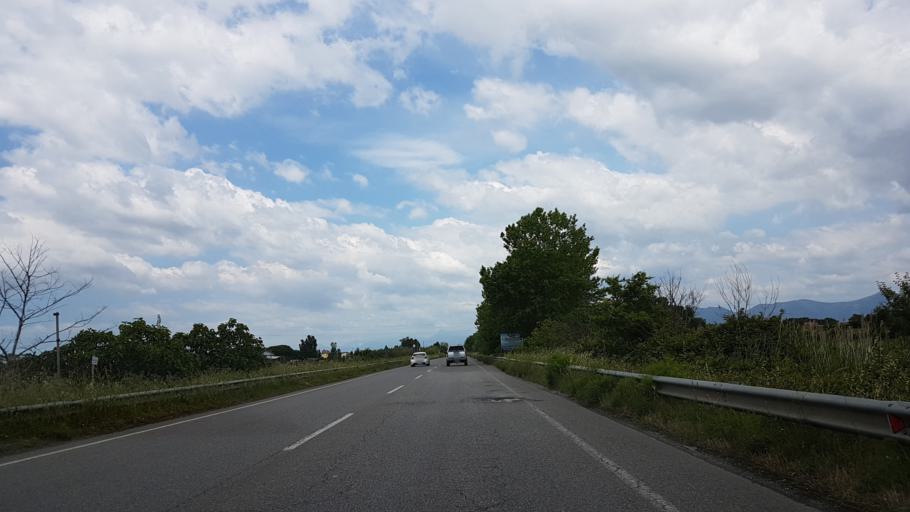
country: IT
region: Tuscany
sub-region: Provincia di Livorno
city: Collesalvetti
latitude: 43.6034
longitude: 10.4752
